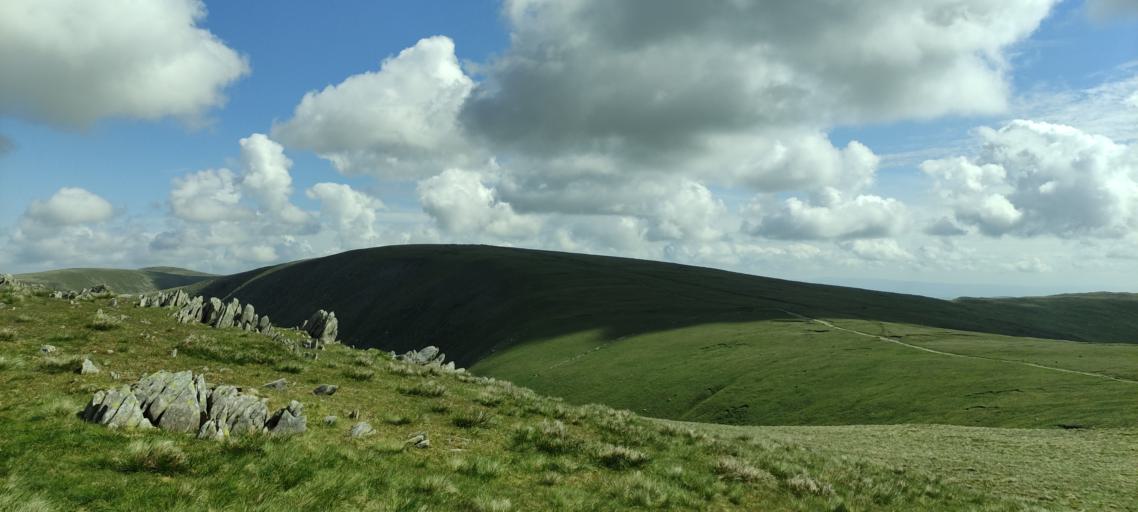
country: GB
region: England
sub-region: Cumbria
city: Ambleside
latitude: 54.4823
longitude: -2.8790
